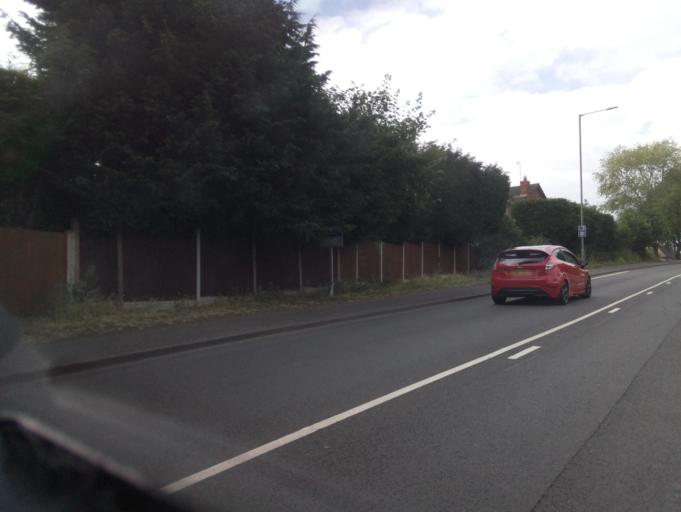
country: GB
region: England
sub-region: Dudley
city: Kingswinford
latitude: 52.5015
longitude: -2.1834
